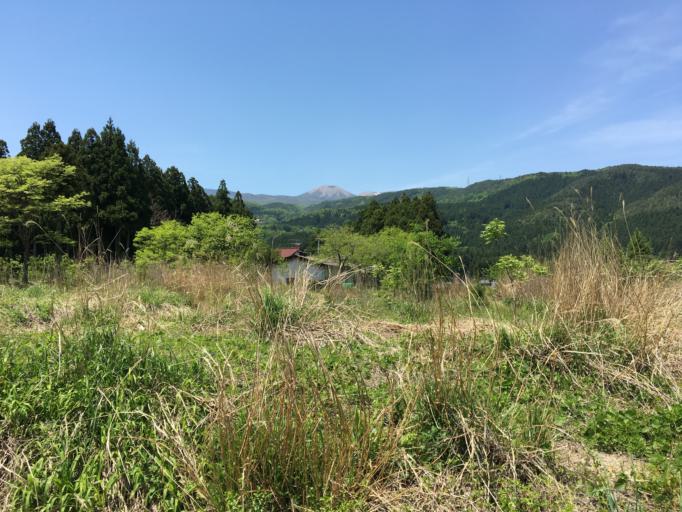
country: JP
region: Fukushima
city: Fukushima-shi
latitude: 37.7146
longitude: 140.3568
